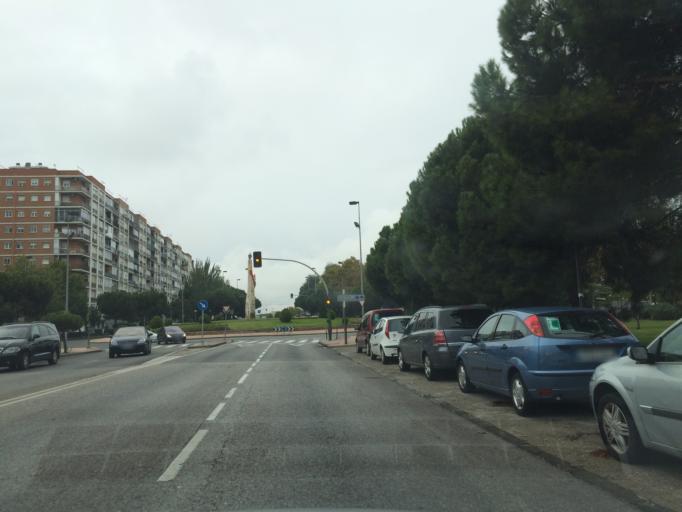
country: ES
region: Madrid
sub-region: Provincia de Madrid
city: Alcorcon
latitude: 40.3530
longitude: -3.8252
